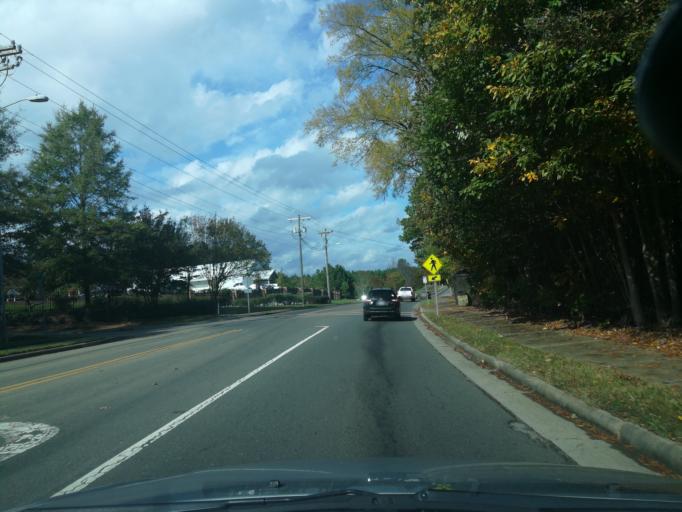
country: US
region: North Carolina
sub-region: Durham County
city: Durham
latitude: 36.0478
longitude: -78.9363
